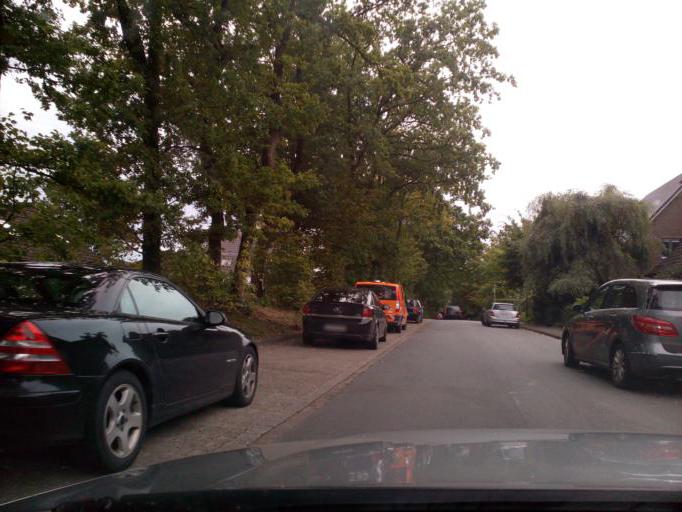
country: DE
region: North Rhine-Westphalia
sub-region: Regierungsbezirk Munster
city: Muenster
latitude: 51.9345
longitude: 7.5927
